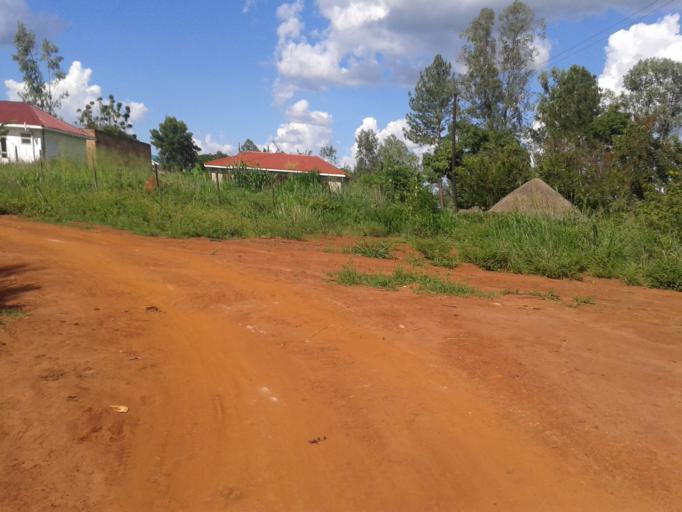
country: UG
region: Northern Region
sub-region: Gulu District
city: Gulu
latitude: 2.7680
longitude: 32.3205
